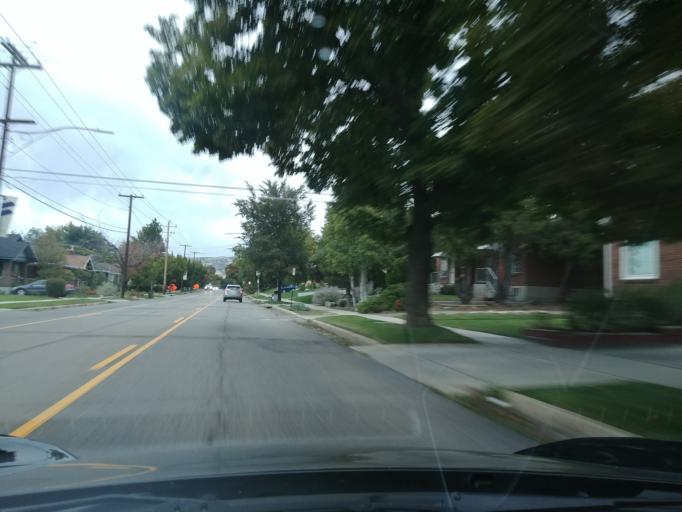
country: US
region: Utah
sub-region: Salt Lake County
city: Willard
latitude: 40.7268
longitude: -111.8539
